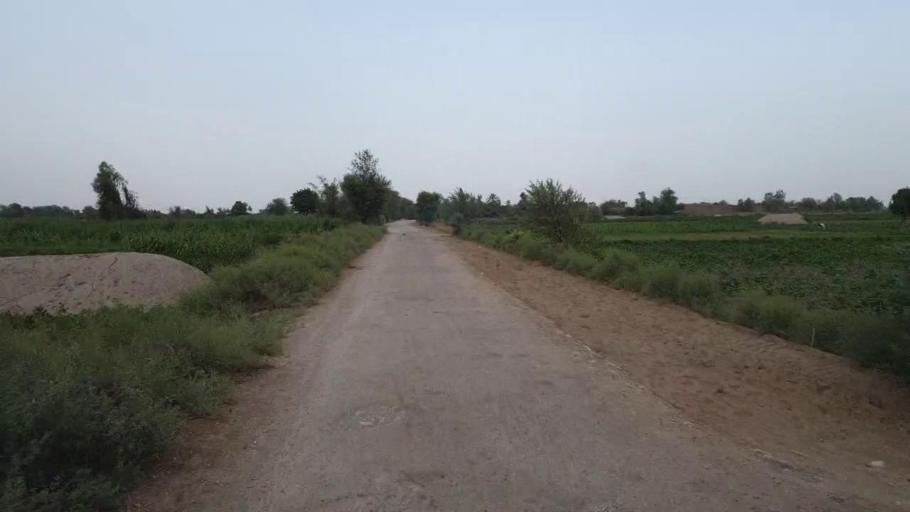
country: PK
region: Sindh
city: Bandhi
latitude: 26.5320
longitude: 68.2047
